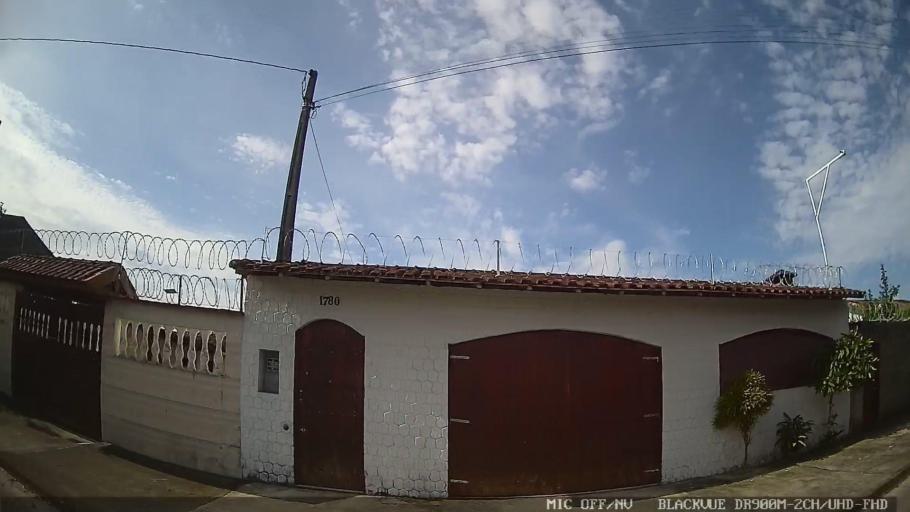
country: BR
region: Sao Paulo
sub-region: Itanhaem
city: Itanhaem
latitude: -24.1559
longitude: -46.7748
